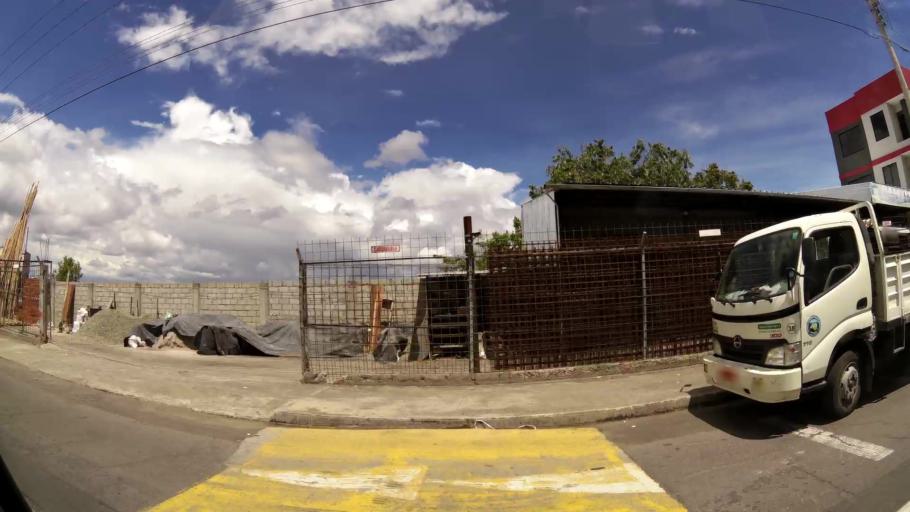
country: EC
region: Tungurahua
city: Ambato
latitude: -1.2790
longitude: -78.6407
